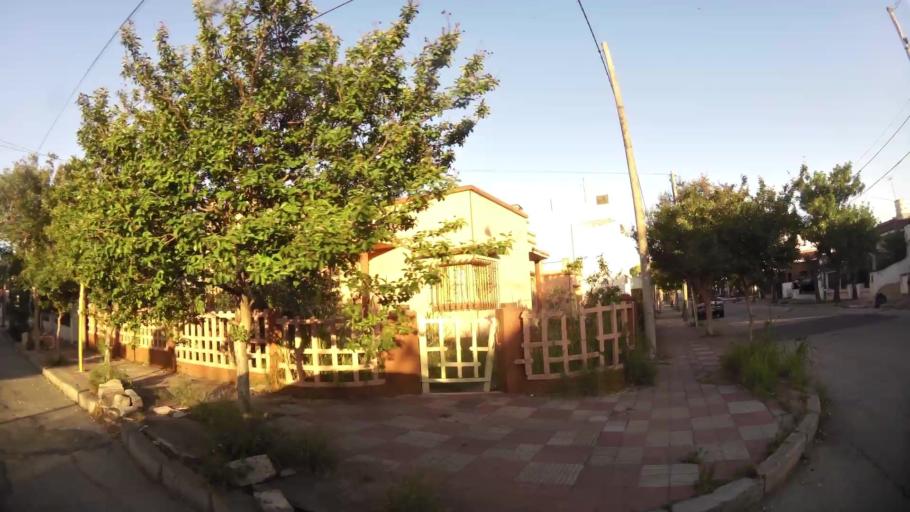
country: AR
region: Cordoba
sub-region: Departamento de Capital
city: Cordoba
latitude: -31.3894
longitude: -64.2118
